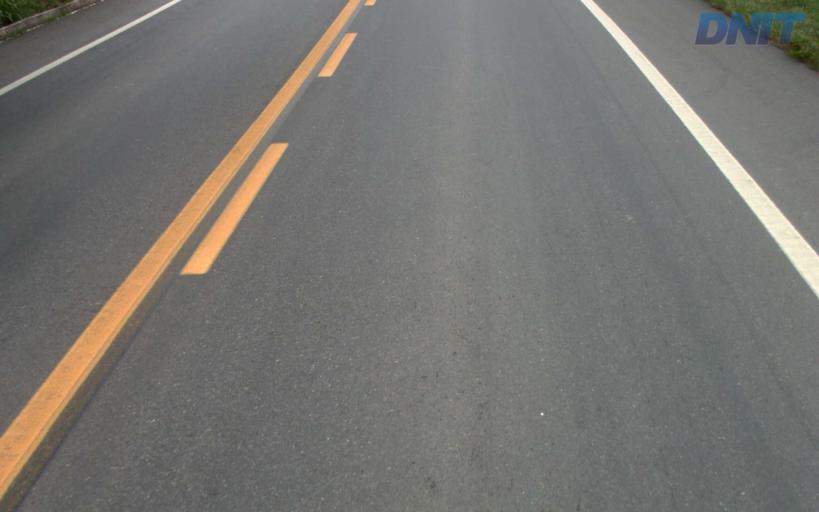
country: BR
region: Minas Gerais
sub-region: Governador Valadares
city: Governador Valadares
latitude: -18.9419
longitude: -42.0596
